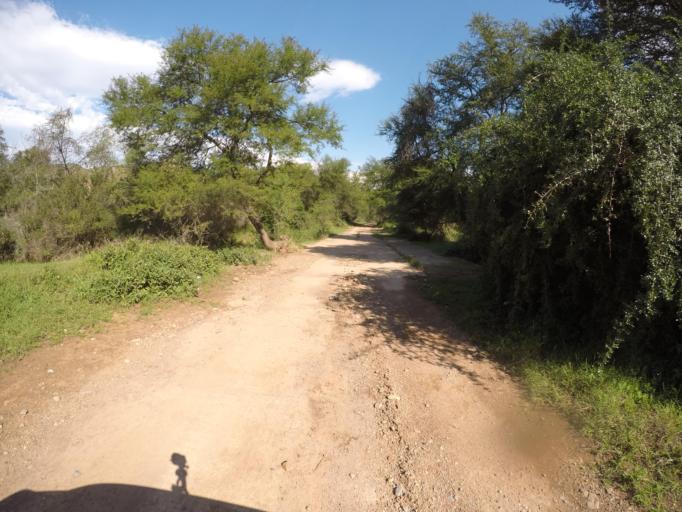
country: ZA
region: Eastern Cape
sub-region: Cacadu District Municipality
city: Kareedouw
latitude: -33.6641
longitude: 24.3889
